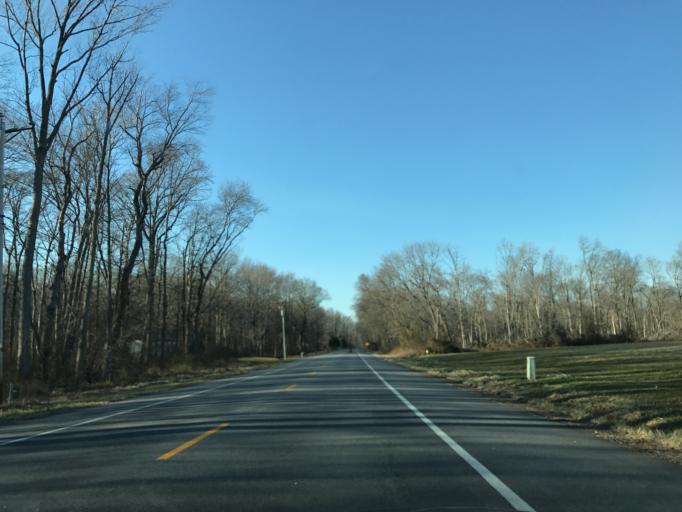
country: US
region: Maryland
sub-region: Queen Anne's County
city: Kingstown
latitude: 39.2292
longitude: -75.8714
